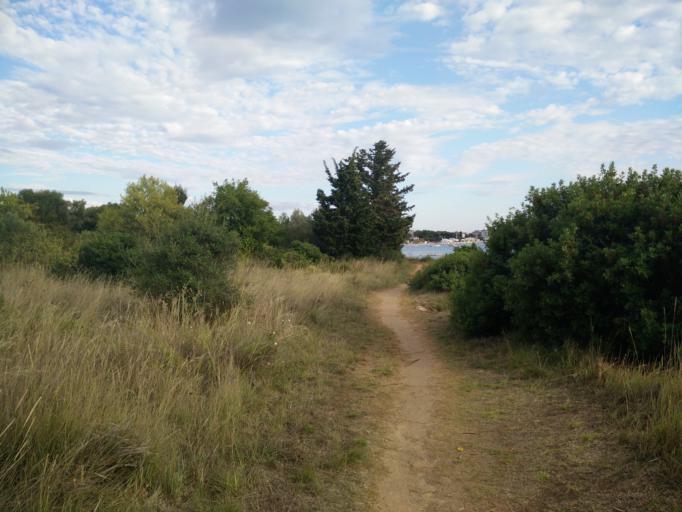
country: HR
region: Zadarska
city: Biograd na Moru
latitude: 43.9505
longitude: 15.4404
